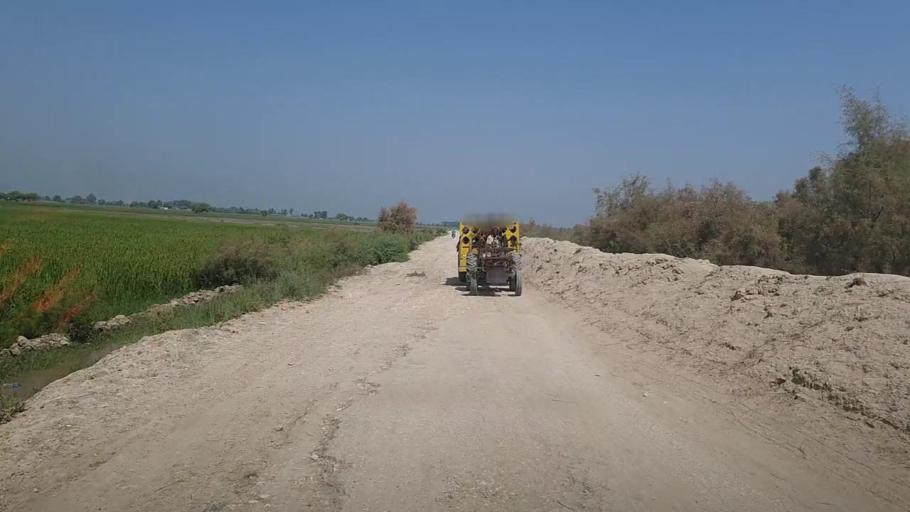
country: PK
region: Sindh
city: Kandhkot
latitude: 28.2967
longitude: 69.2918
